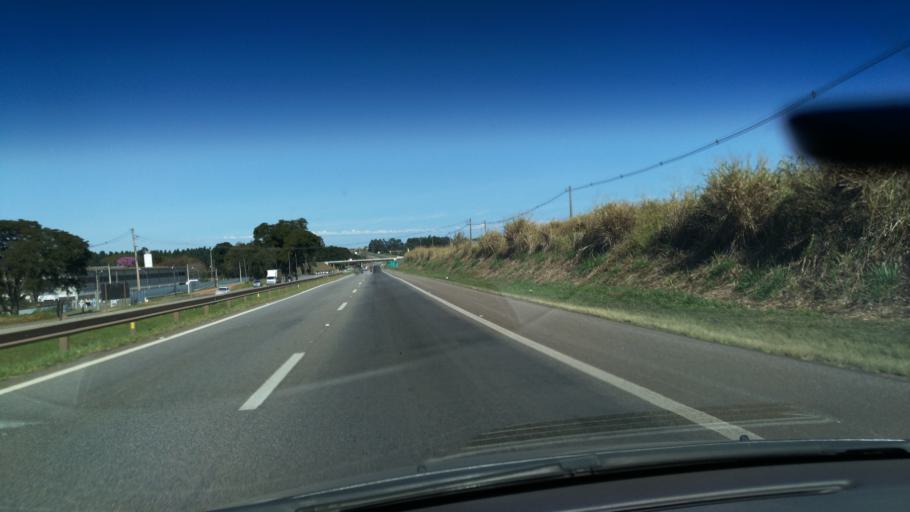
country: BR
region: Sao Paulo
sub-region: Santo Antonio De Posse
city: Santo Antonio de Posse
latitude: -22.6147
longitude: -47.0073
